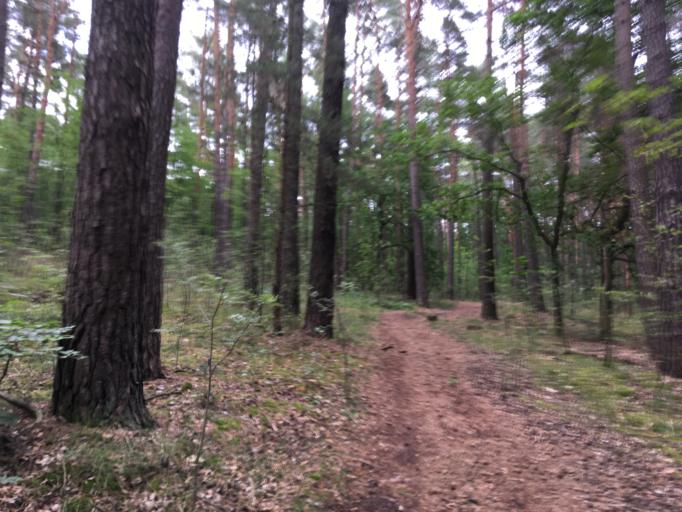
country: DE
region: Brandenburg
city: Bernau bei Berlin
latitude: 52.6898
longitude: 13.5354
